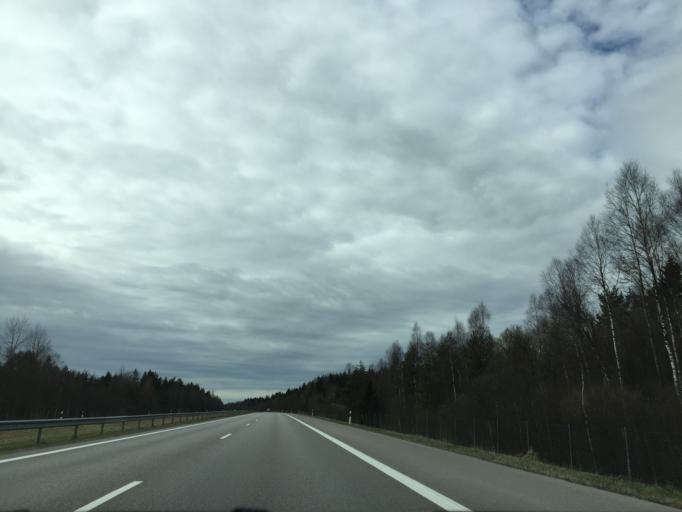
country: LT
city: Silale
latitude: 55.6058
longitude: 22.0898
